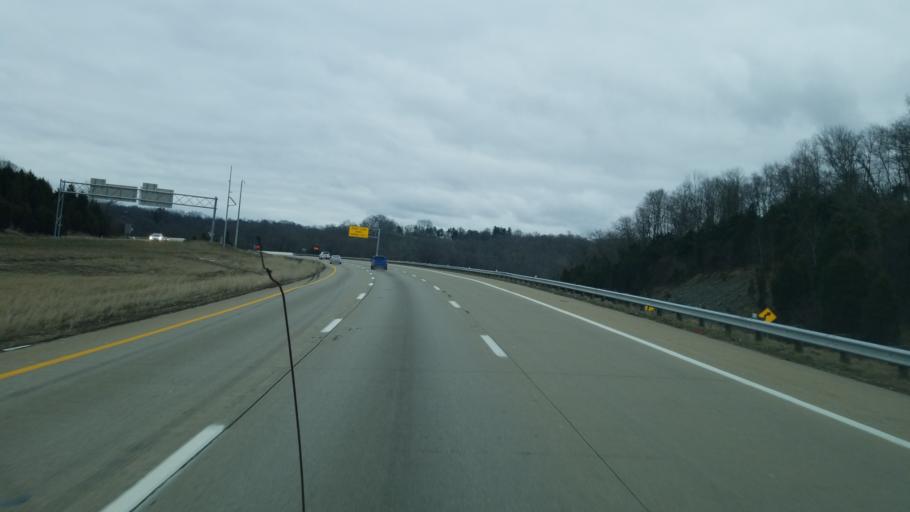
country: US
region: Kentucky
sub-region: Campbell County
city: Silver Grove
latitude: 39.0546
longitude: -84.3952
